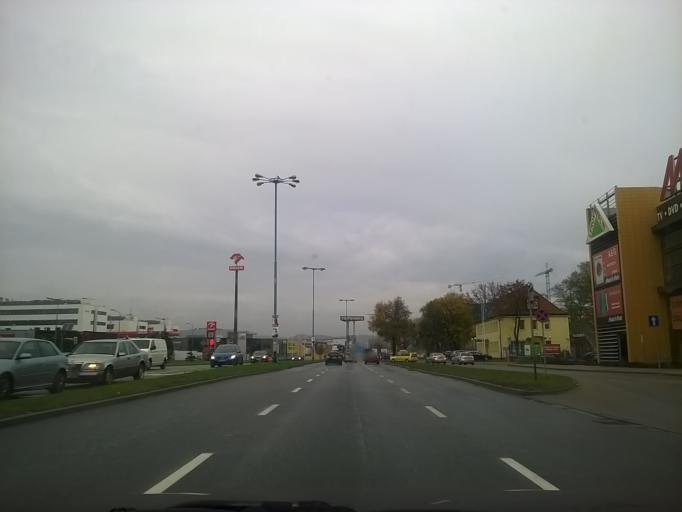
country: PL
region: Pomeranian Voivodeship
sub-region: Sopot
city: Sopot
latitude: 54.3943
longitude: 18.5811
